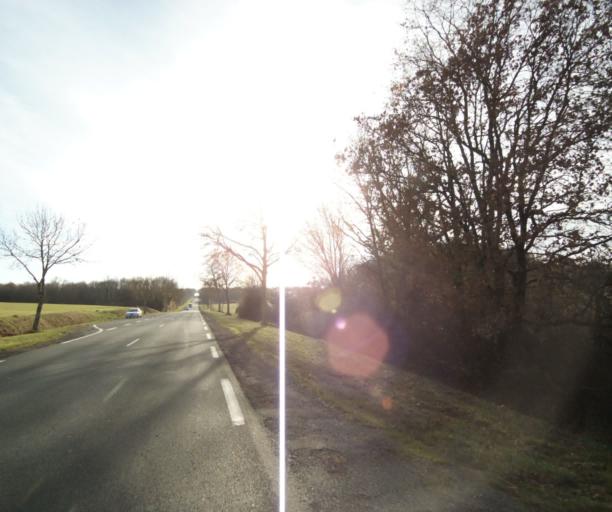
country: FR
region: Poitou-Charentes
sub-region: Departement de la Charente-Maritime
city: Saint-Hilaire-de-Villefranche
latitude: 45.8279
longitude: -0.5413
